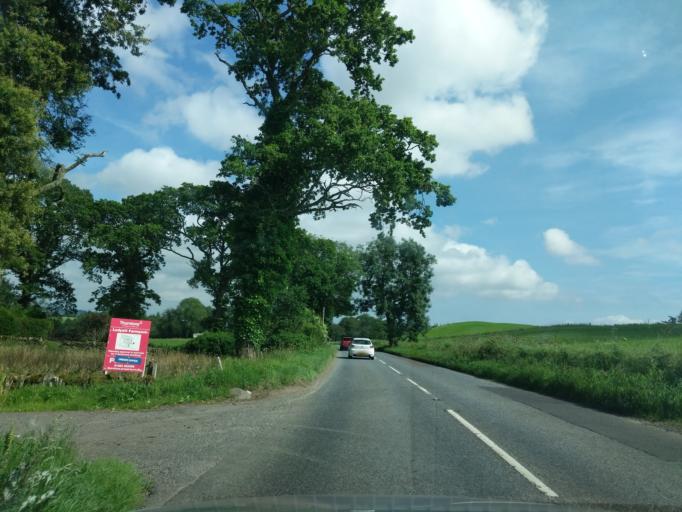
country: GB
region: Scotland
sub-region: Angus
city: Muirhead
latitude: 56.5068
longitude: -3.1487
